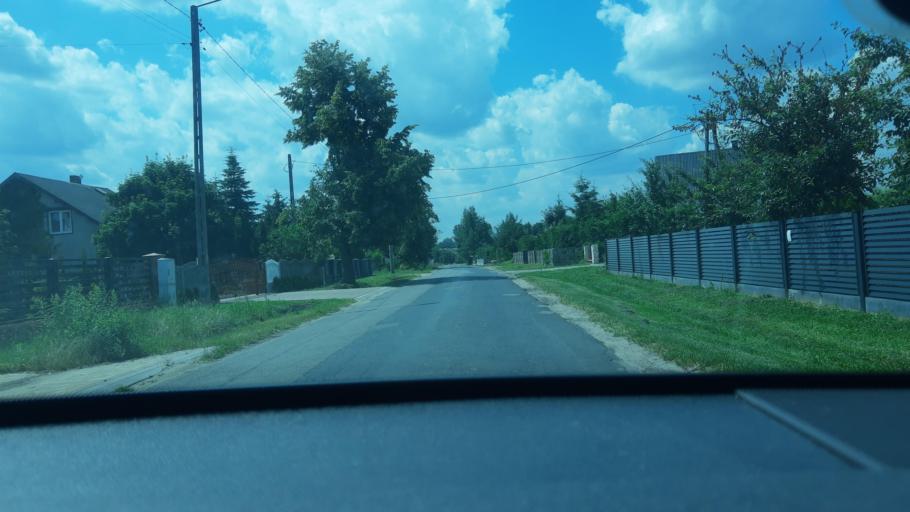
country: PL
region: Lodz Voivodeship
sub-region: Powiat sieradzki
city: Sieradz
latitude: 51.5496
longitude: 18.7578
